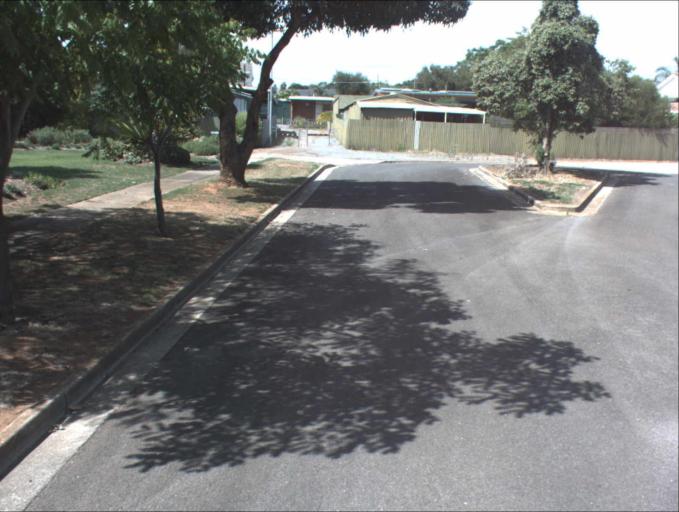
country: AU
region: South Australia
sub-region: Salisbury
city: Ingle Farm
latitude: -34.8438
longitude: 138.6219
